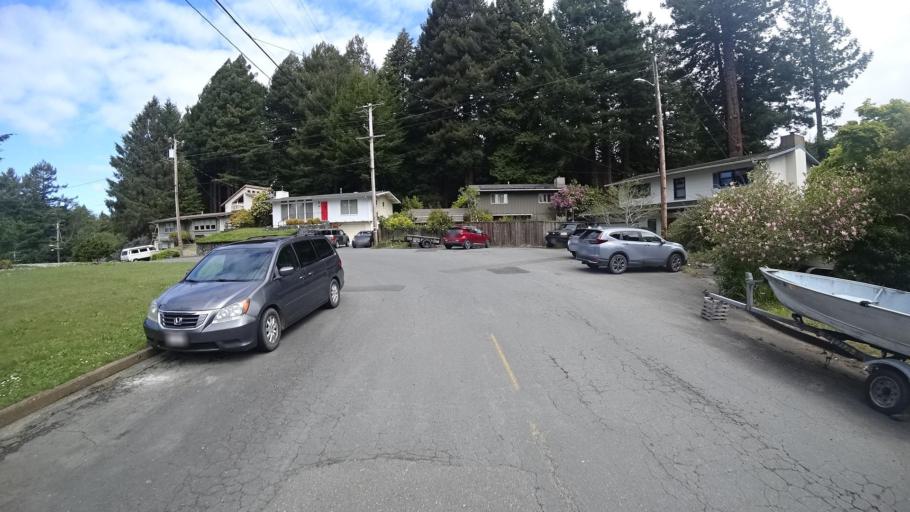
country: US
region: California
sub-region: Humboldt County
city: Arcata
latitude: 40.8641
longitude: -124.0694
